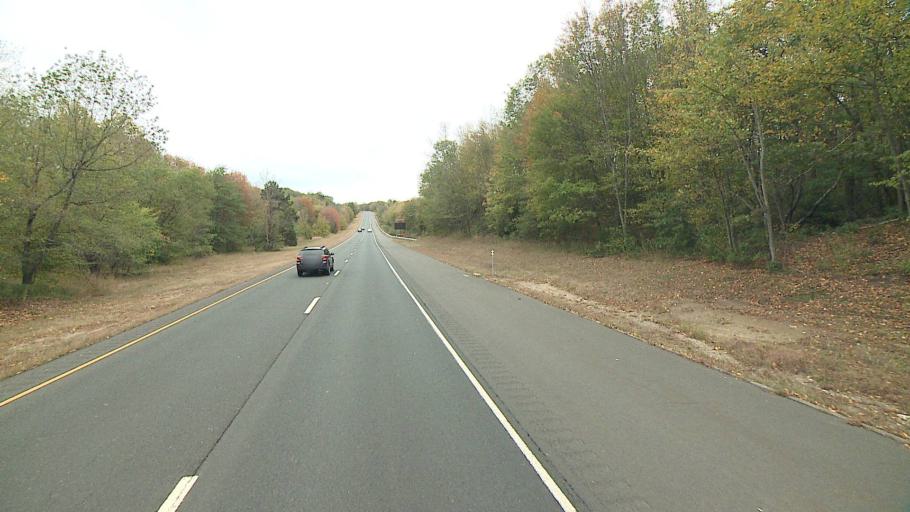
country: US
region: Connecticut
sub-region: Middlesex County
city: East Haddam
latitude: 41.4417
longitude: -72.5186
